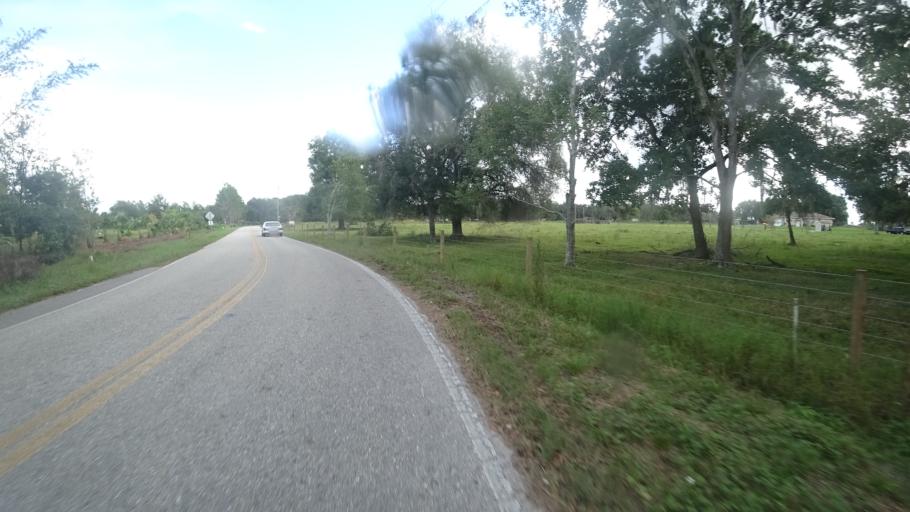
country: US
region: Florida
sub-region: Hillsborough County
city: Wimauma
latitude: 27.5972
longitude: -82.2077
